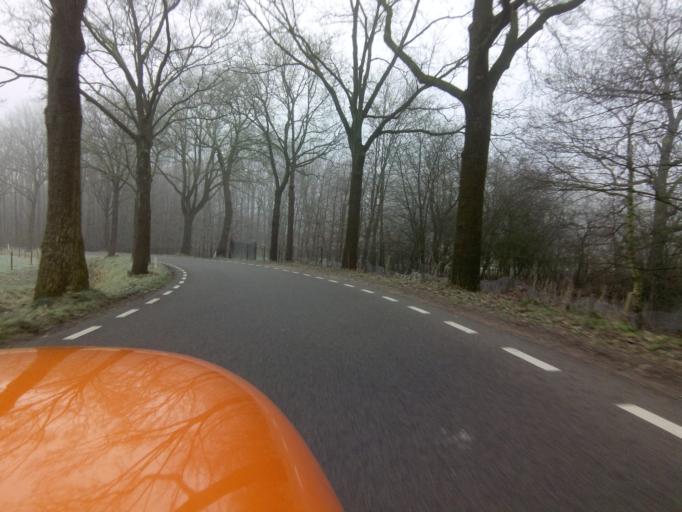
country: NL
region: Utrecht
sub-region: Gemeente Leusden
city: Leusden
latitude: 52.1562
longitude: 5.4600
